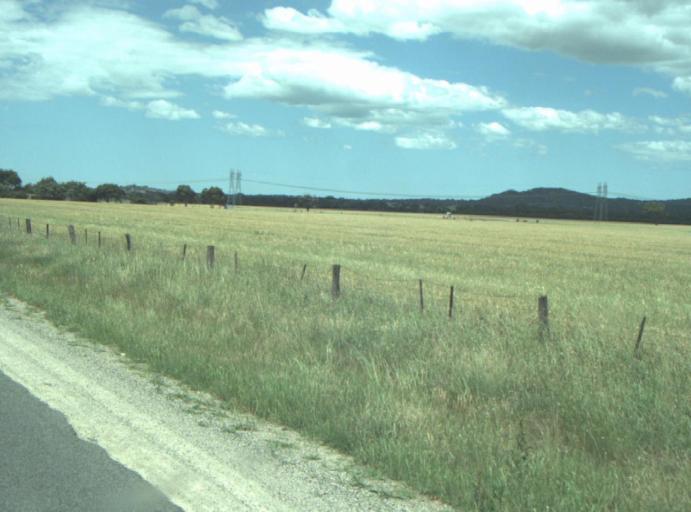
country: AU
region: Victoria
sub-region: Wyndham
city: Little River
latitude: -37.8749
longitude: 144.3918
